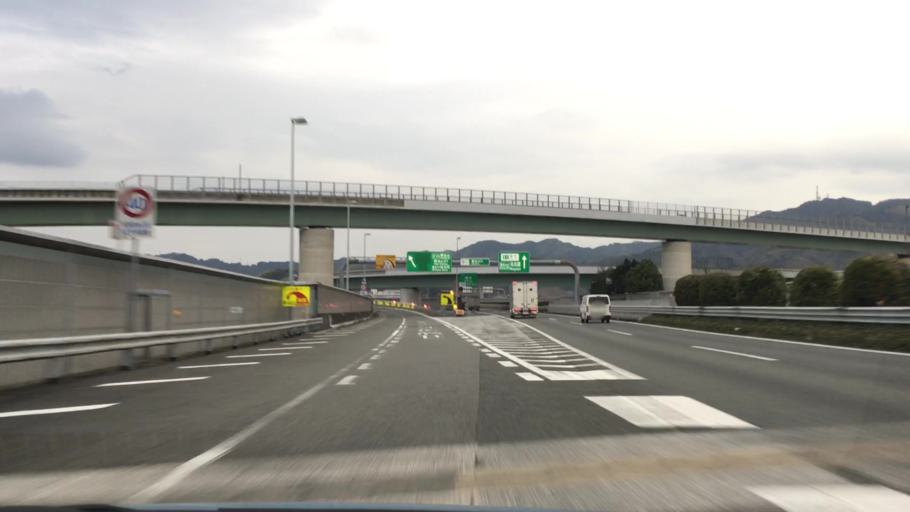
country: JP
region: Shizuoka
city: Shizuoka-shi
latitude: 35.0468
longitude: 138.4898
